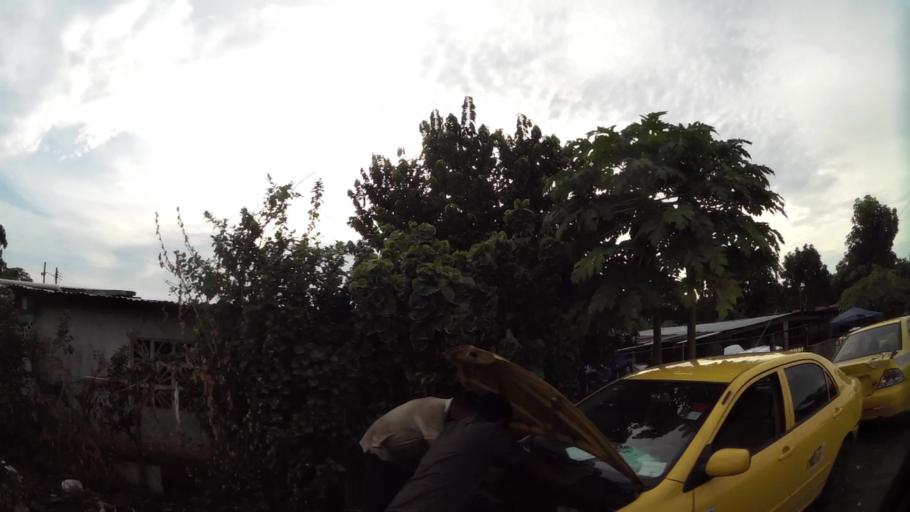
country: PA
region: Panama
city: Tocumen
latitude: 9.0920
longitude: -79.3808
